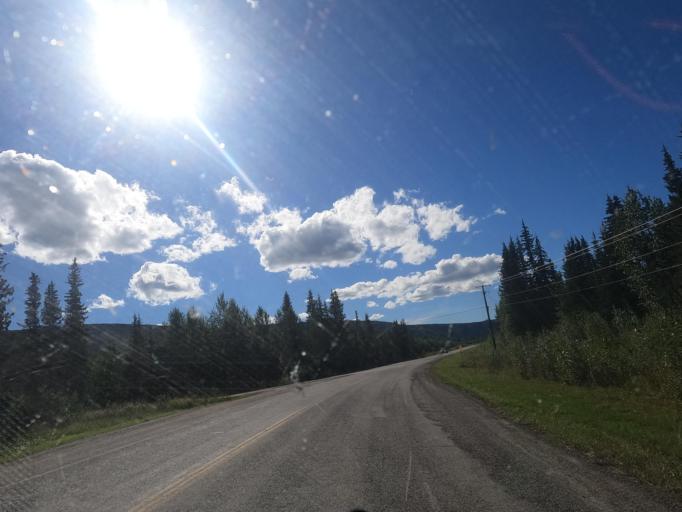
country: CA
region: Yukon
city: Dawson City
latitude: 64.0315
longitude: -139.1684
